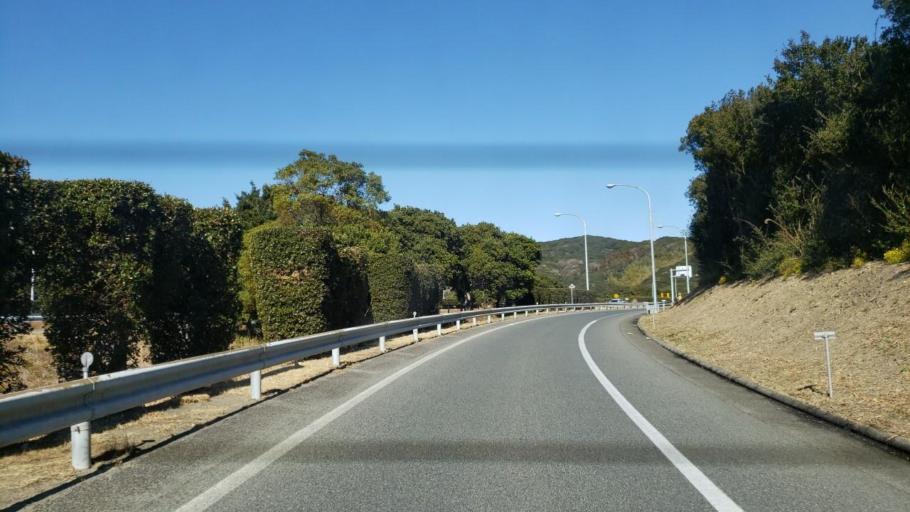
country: JP
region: Tokushima
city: Narutocho-mitsuishi
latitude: 34.2208
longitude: 134.6270
